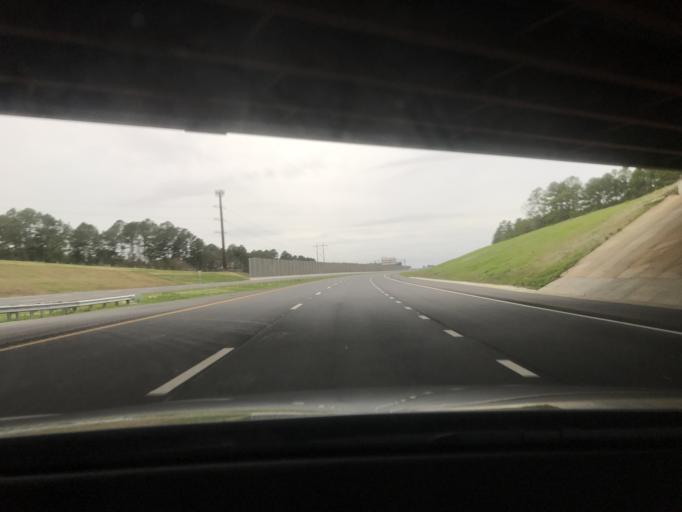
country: US
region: North Carolina
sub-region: Cumberland County
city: Fort Bragg
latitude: 35.1074
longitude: -78.9969
